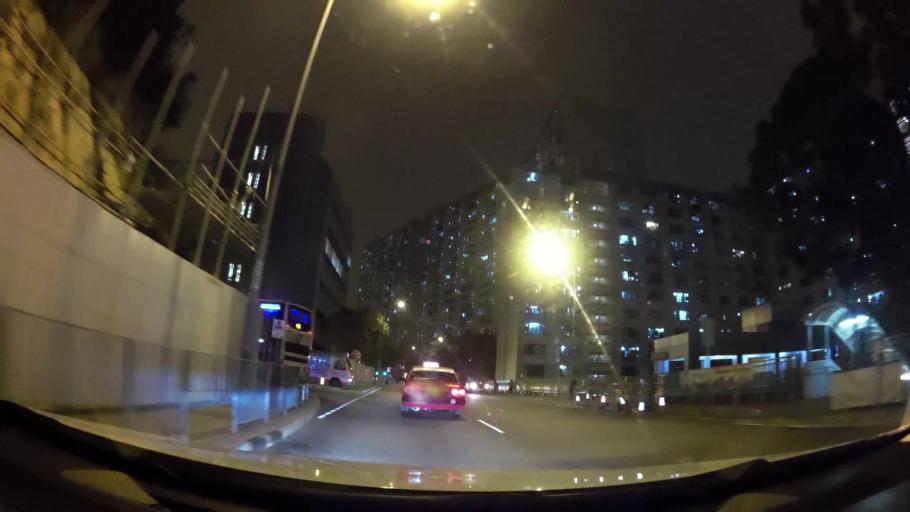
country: HK
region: Tsuen Wan
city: Tsuen Wan
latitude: 22.3474
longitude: 114.1267
